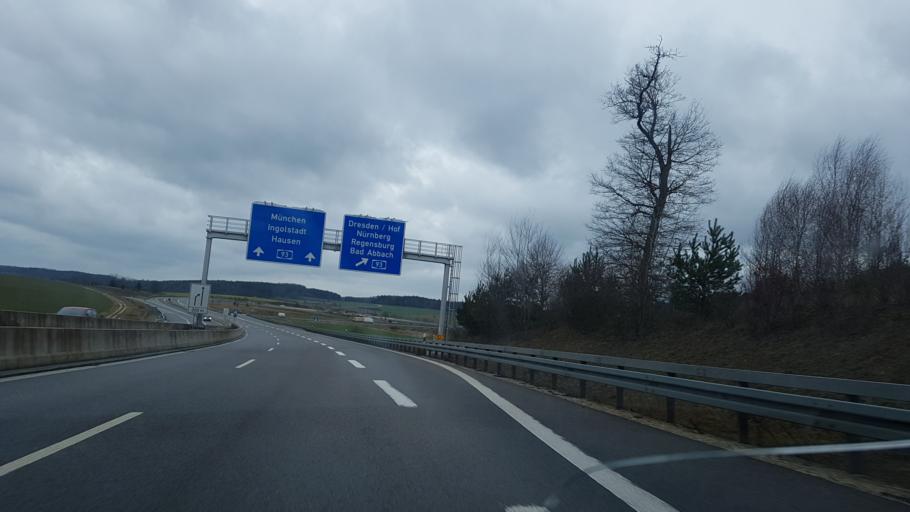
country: DE
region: Bavaria
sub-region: Lower Bavaria
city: Bad Abbach
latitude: 48.8880
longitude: 12.0815
